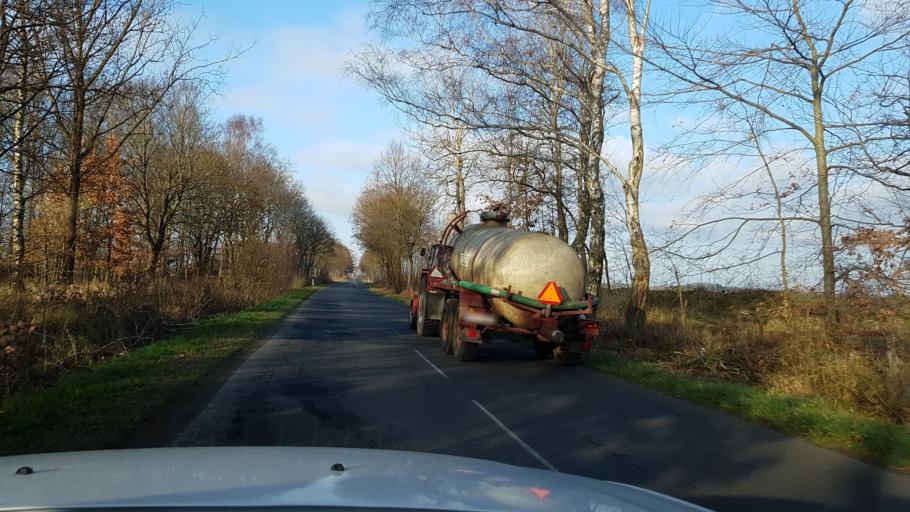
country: PL
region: West Pomeranian Voivodeship
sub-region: Powiat stargardzki
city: Chociwel
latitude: 53.4460
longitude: 15.3494
